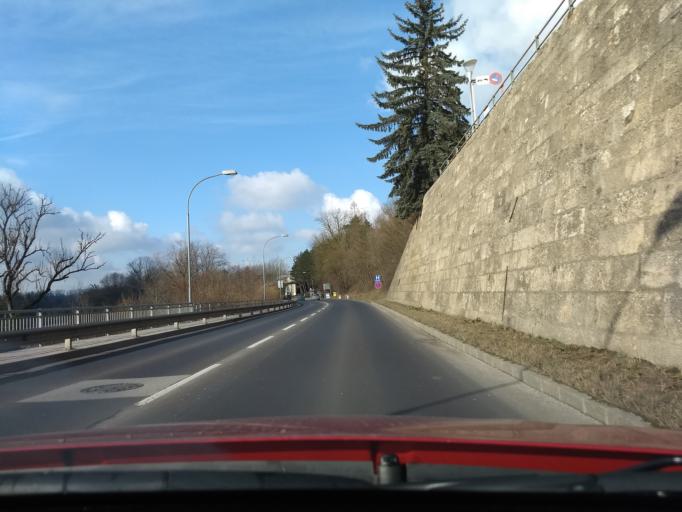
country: AT
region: Upper Austria
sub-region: Politischer Bezirk Steyr-Land
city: Garsten
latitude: 48.0430
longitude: 14.3947
